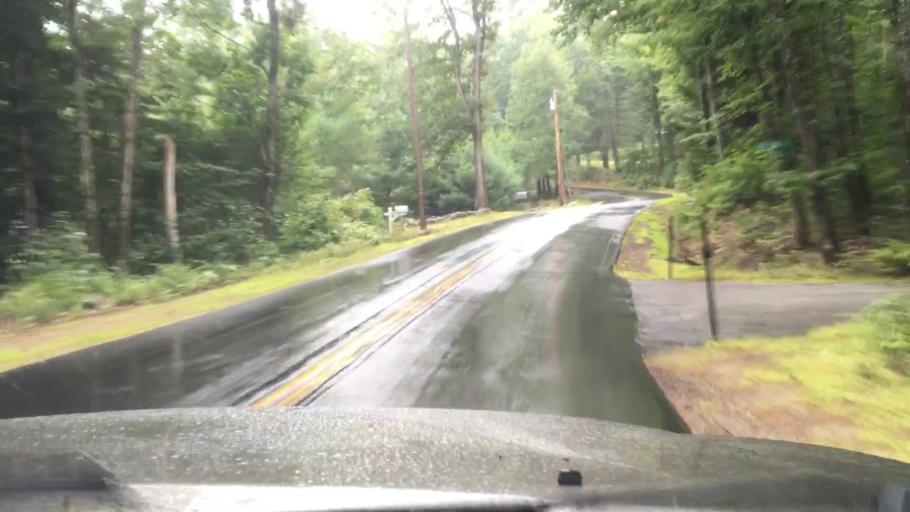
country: US
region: New Hampshire
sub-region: Belknap County
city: Meredith
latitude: 43.6885
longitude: -71.5140
